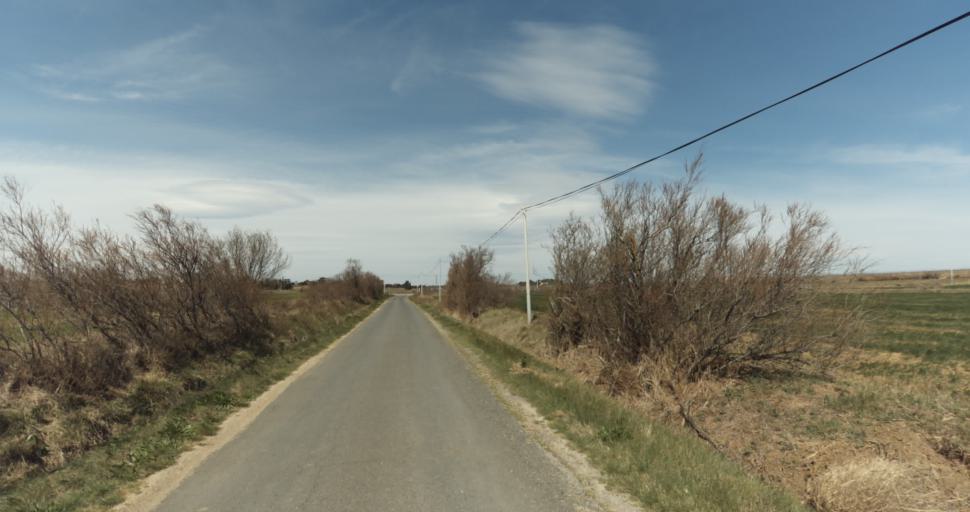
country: FR
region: Languedoc-Roussillon
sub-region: Departement de l'Herault
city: Marseillan
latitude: 43.3859
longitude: 3.5501
